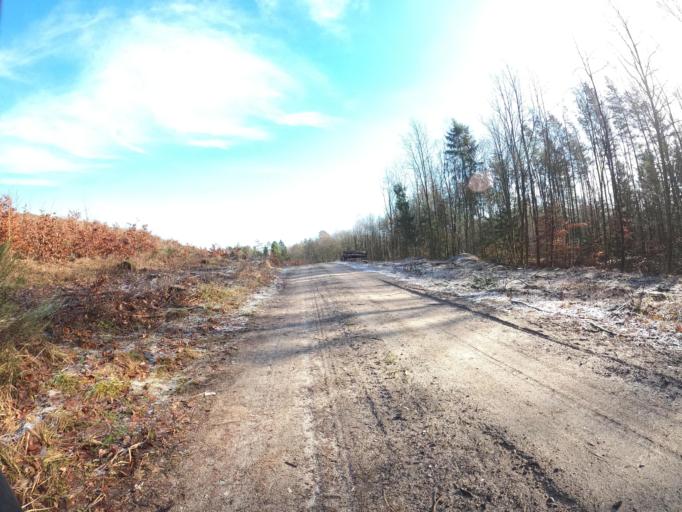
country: PL
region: West Pomeranian Voivodeship
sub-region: Powiat koszalinski
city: Polanow
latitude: 54.1173
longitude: 16.7603
